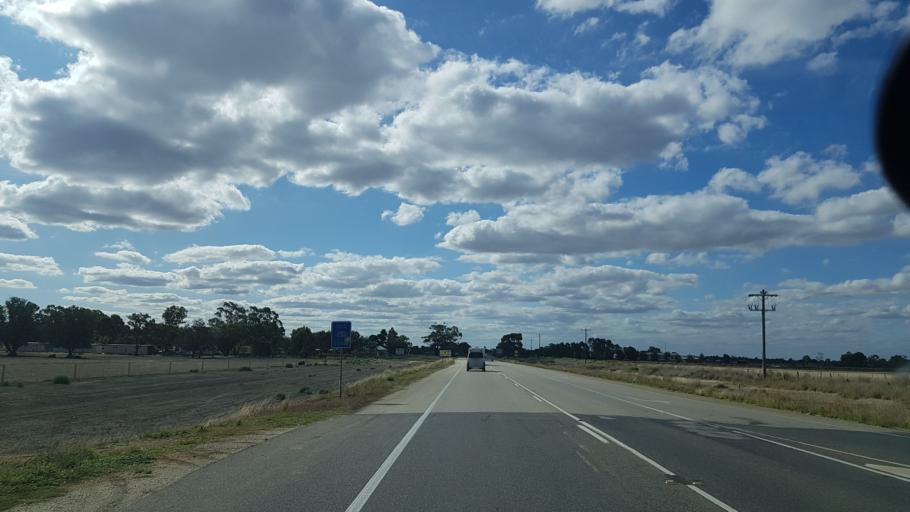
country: AU
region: Victoria
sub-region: Swan Hill
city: Swan Hill
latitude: -35.7628
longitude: 143.9310
